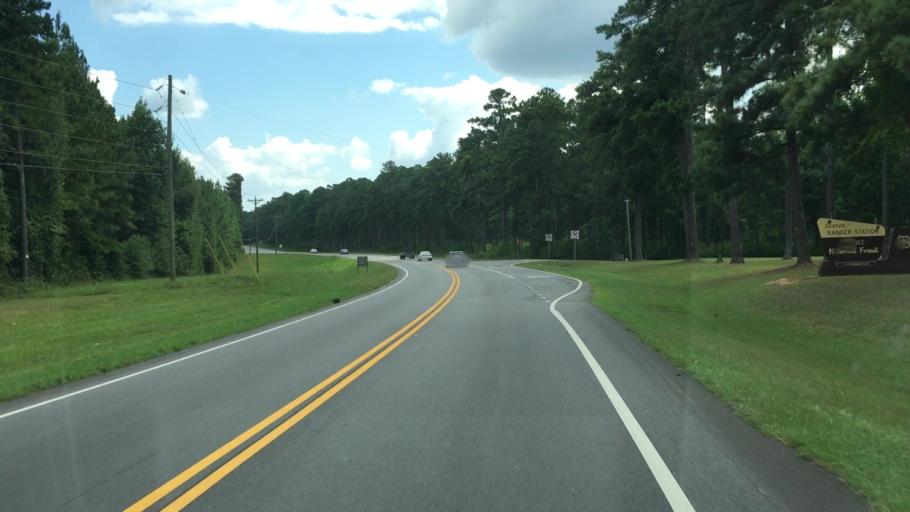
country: US
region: Georgia
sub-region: Putnam County
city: Jefferson
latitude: 33.4139
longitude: -83.3722
